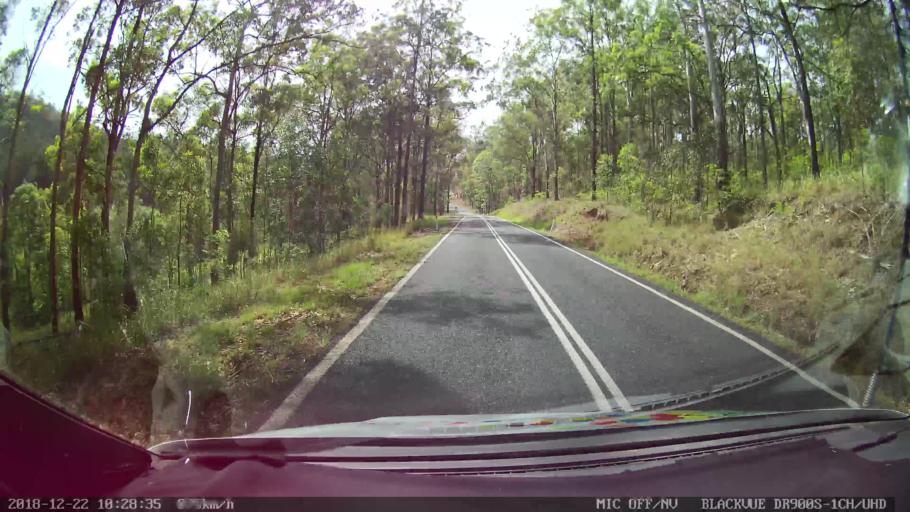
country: AU
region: New South Wales
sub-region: Clarence Valley
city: Gordon
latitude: -29.6055
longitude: 152.5929
